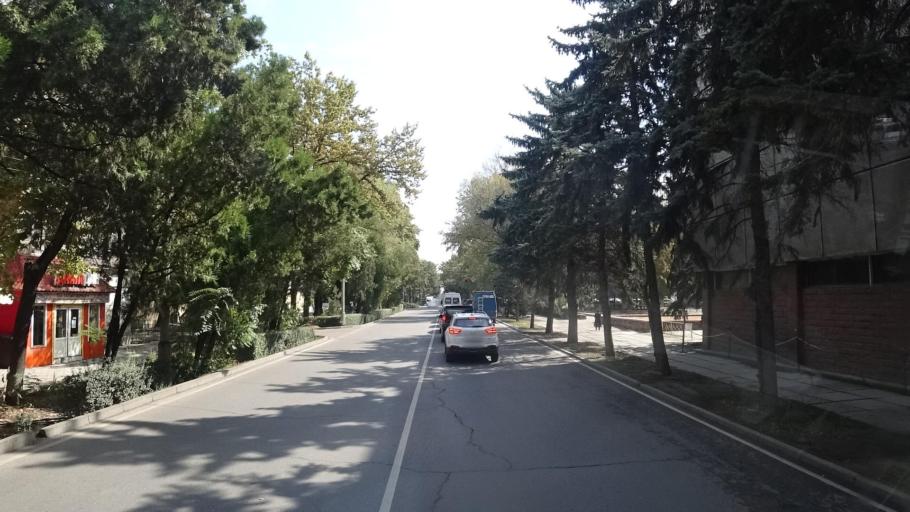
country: KG
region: Chuy
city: Bishkek
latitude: 42.8807
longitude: 74.6055
